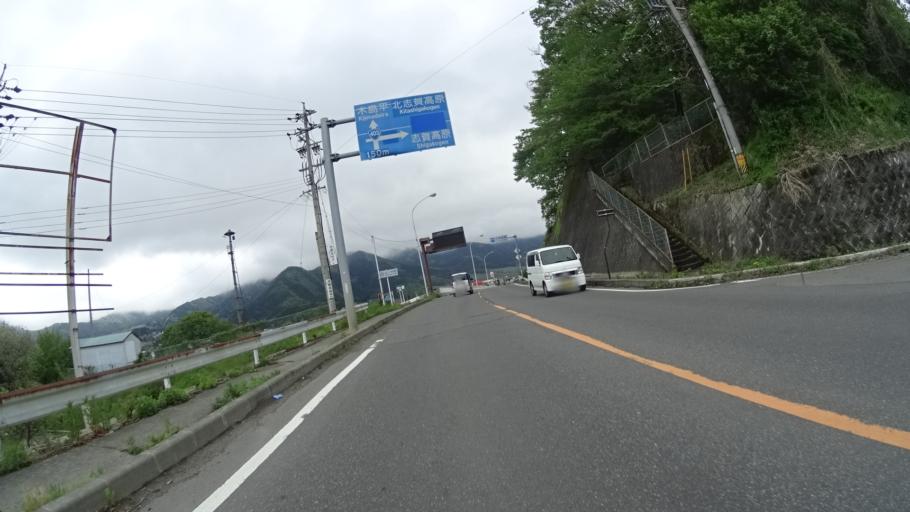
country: JP
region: Nagano
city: Nakano
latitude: 36.7589
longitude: 138.3962
